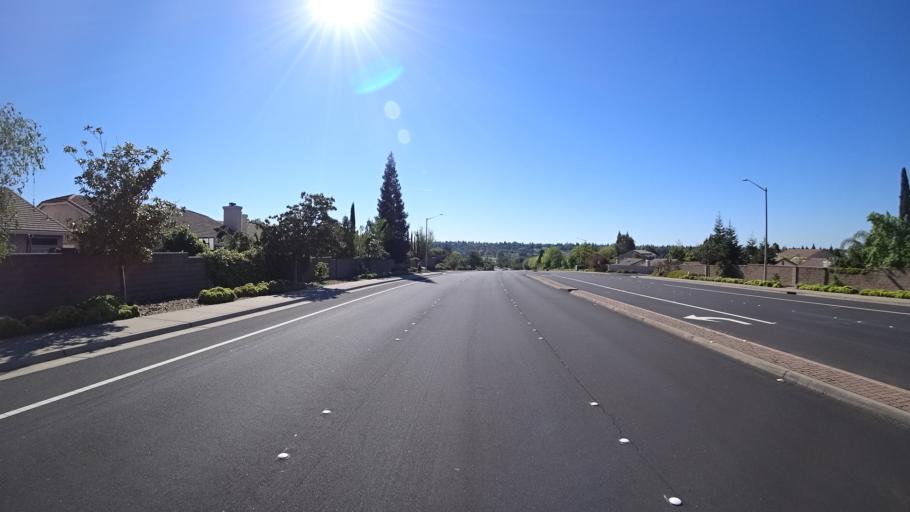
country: US
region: California
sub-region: Placer County
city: Rocklin
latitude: 38.8179
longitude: -121.2722
